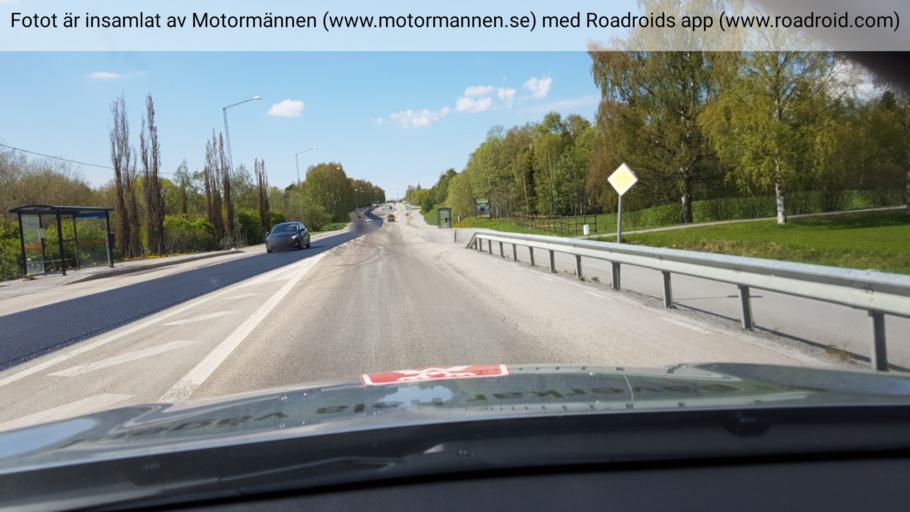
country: SE
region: Jaemtland
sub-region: OEstersunds Kommun
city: Ostersund
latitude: 63.1503
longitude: 14.7037
